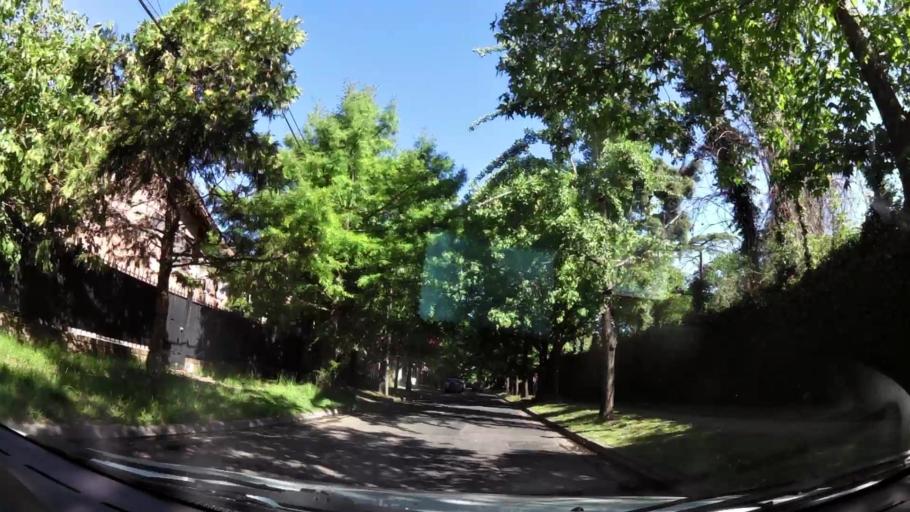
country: AR
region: Buenos Aires
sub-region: Partido de San Isidro
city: San Isidro
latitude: -34.4780
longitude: -58.5481
